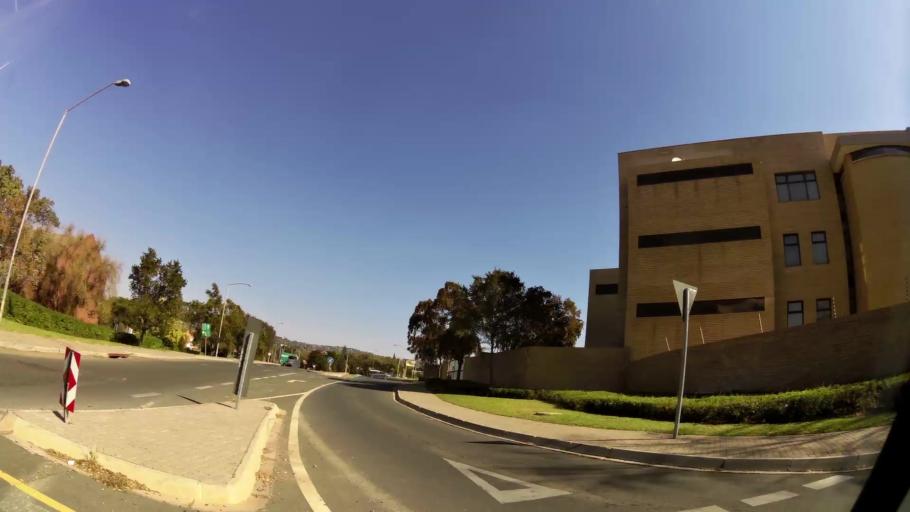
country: ZA
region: Gauteng
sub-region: City of Tshwane Metropolitan Municipality
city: Pretoria
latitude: -25.7740
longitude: 28.2689
